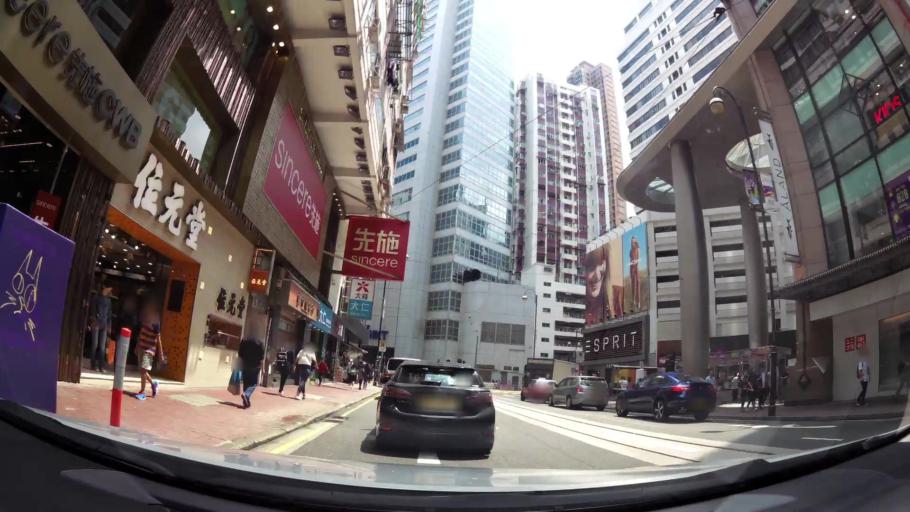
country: HK
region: Wanchai
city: Wan Chai
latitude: 22.2785
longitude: 114.1839
